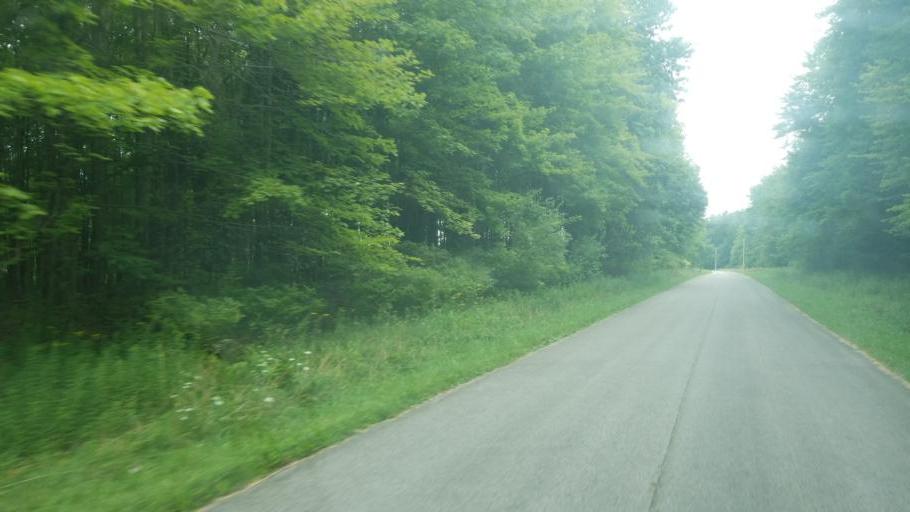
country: US
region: Pennsylvania
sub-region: Crawford County
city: Pymatuning Central
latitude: 41.6303
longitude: -80.4970
